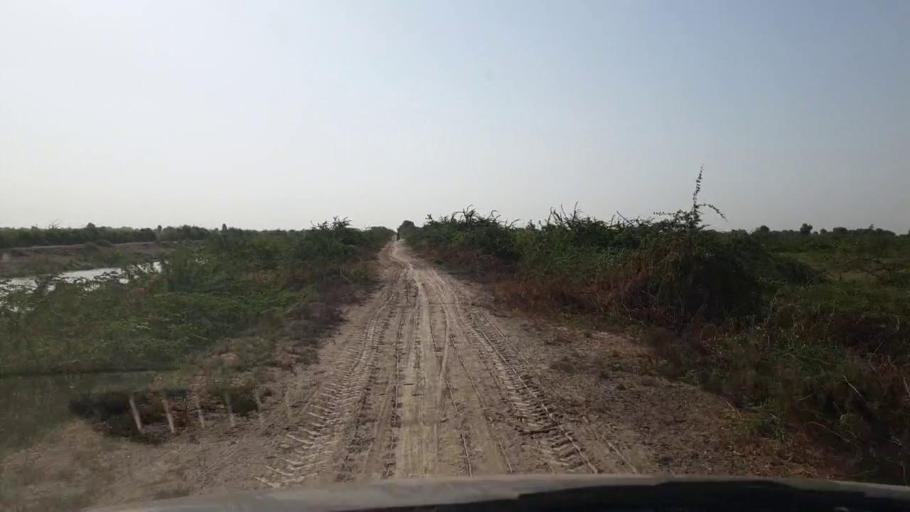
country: PK
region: Sindh
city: Kadhan
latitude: 24.5909
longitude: 69.0766
